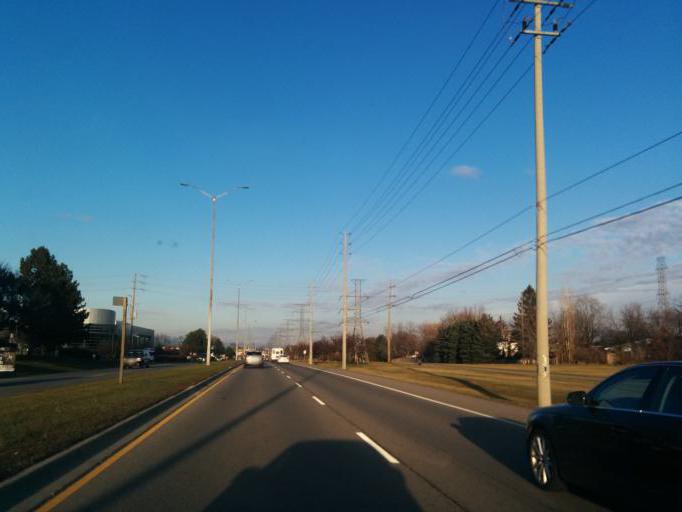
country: CA
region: Ontario
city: Etobicoke
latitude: 43.5938
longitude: -79.5861
